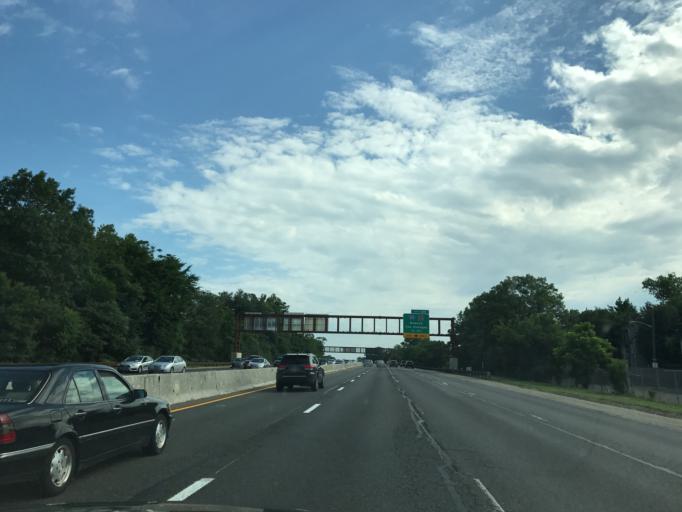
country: US
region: New Jersey
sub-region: Essex County
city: Irvington
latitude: 40.7400
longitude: -74.2160
